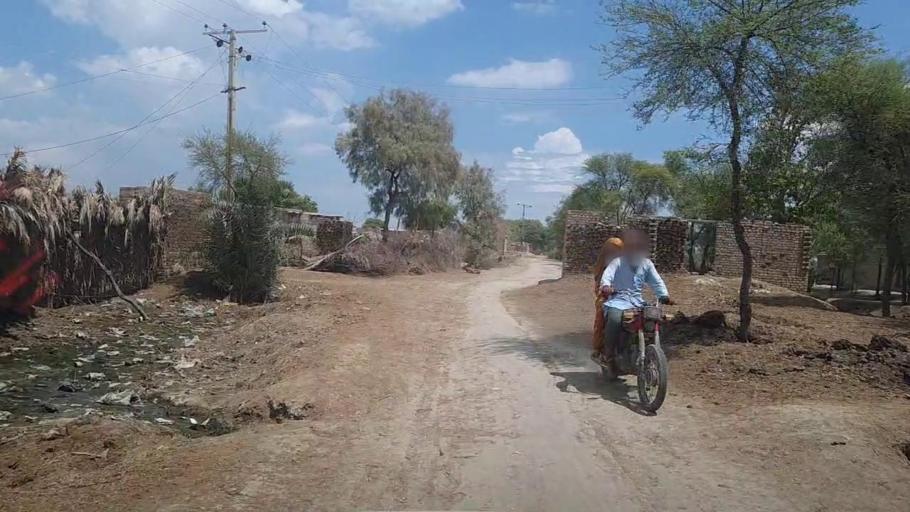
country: PK
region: Sindh
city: Kandhkot
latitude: 28.3400
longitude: 69.2538
